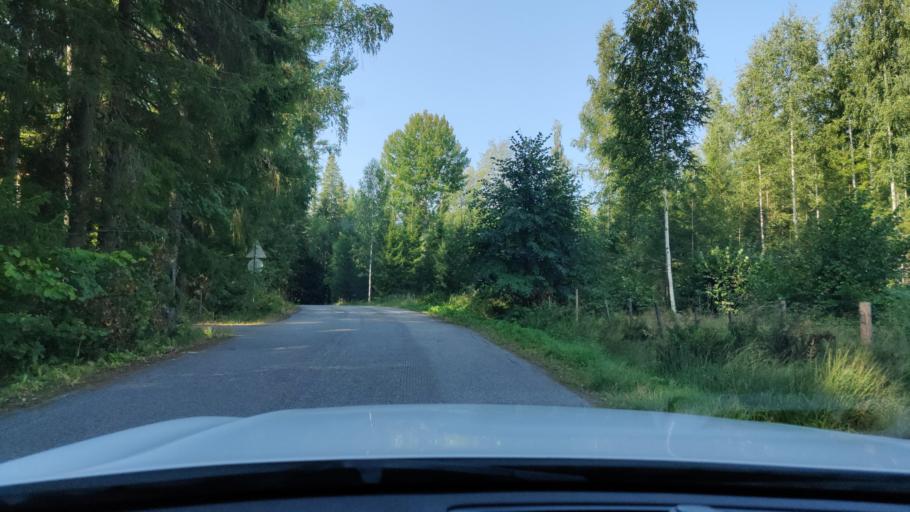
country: FI
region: Haeme
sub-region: Haemeenlinna
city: Tervakoski
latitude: 60.6738
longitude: 24.6392
